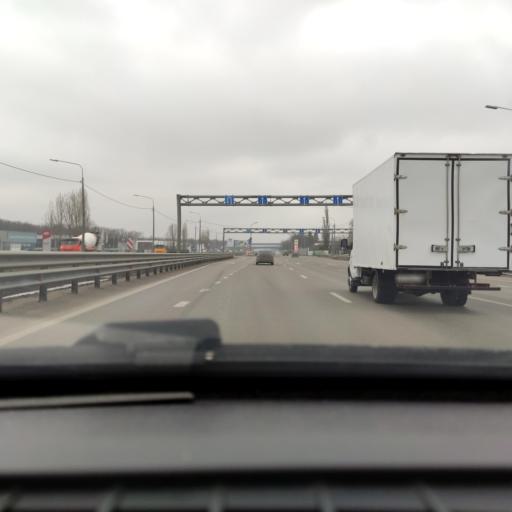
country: RU
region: Voronezj
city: Podgornoye
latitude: 51.7778
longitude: 39.1939
